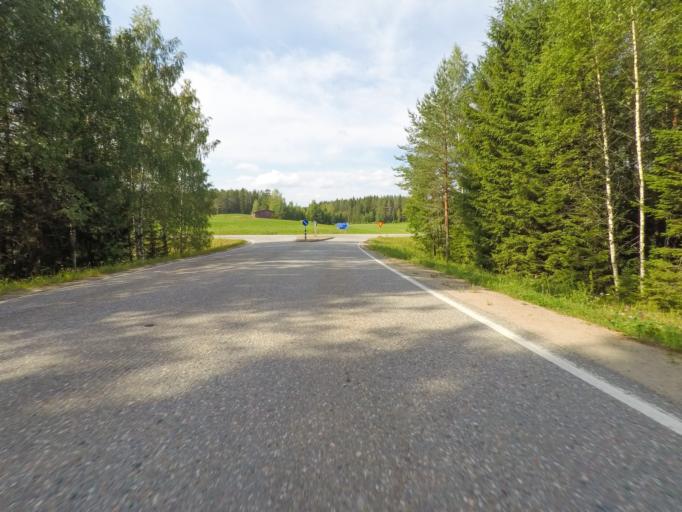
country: FI
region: Southern Savonia
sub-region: Savonlinna
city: Sulkava
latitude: 61.7899
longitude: 28.2427
